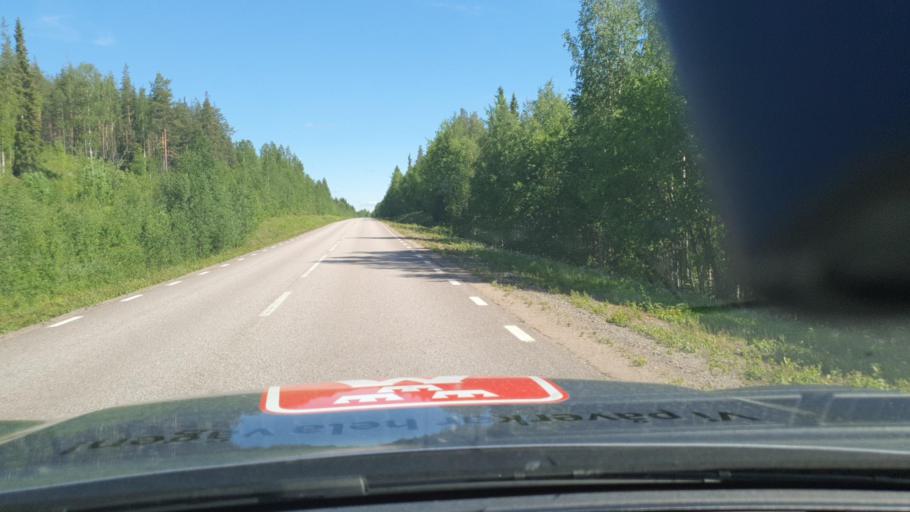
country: SE
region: Norrbotten
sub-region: Overkalix Kommun
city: OEverkalix
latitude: 66.7969
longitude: 22.7279
